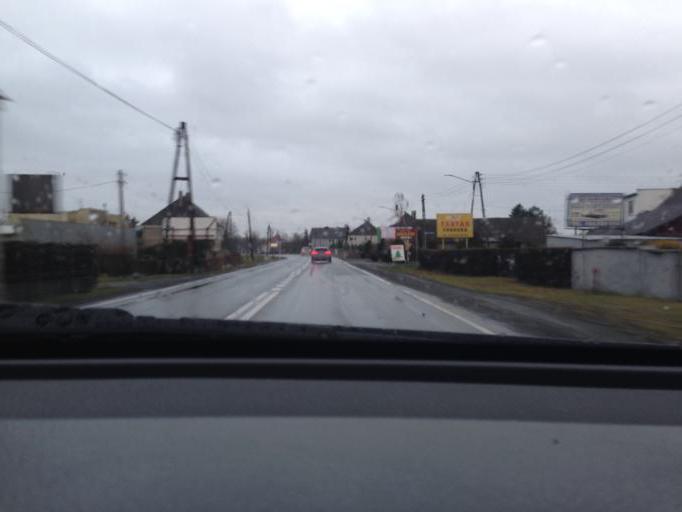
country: PL
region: Opole Voivodeship
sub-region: Powiat opolski
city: Wegry
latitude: 50.7113
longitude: 17.9893
